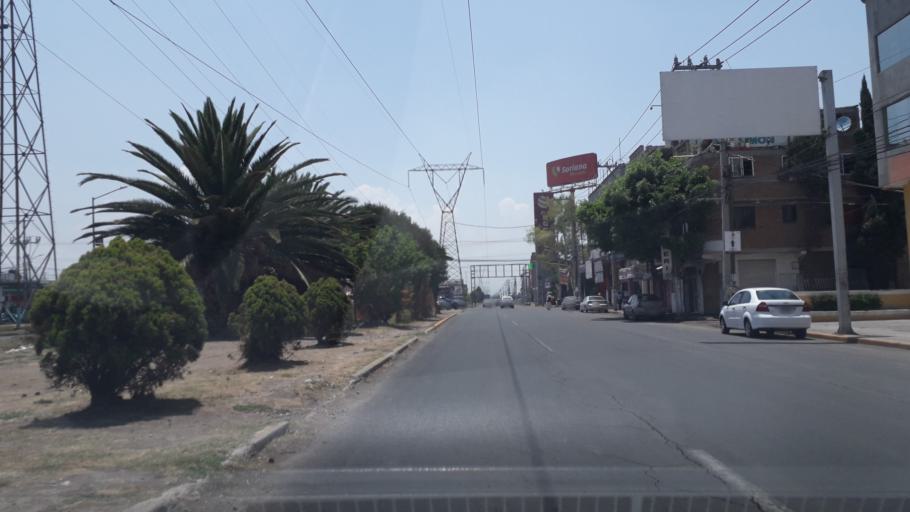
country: MX
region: Mexico
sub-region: Tultitlan
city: Fuentes del Valle
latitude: 19.6408
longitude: -99.1344
